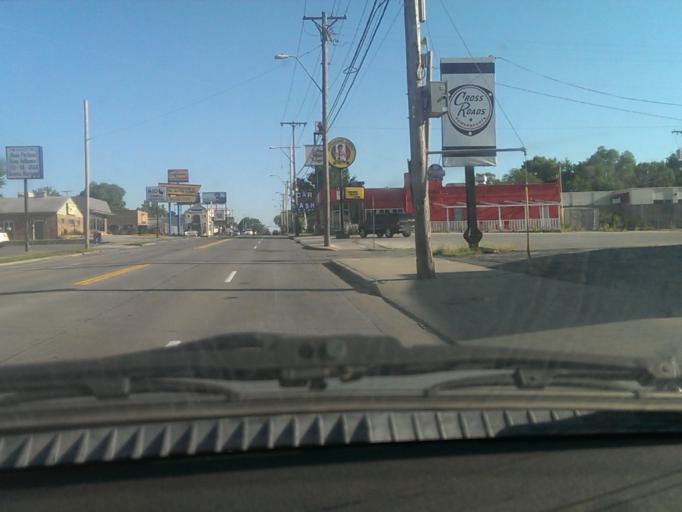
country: US
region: Kansas
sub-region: Johnson County
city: Leawood
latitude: 38.9775
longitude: -94.5949
